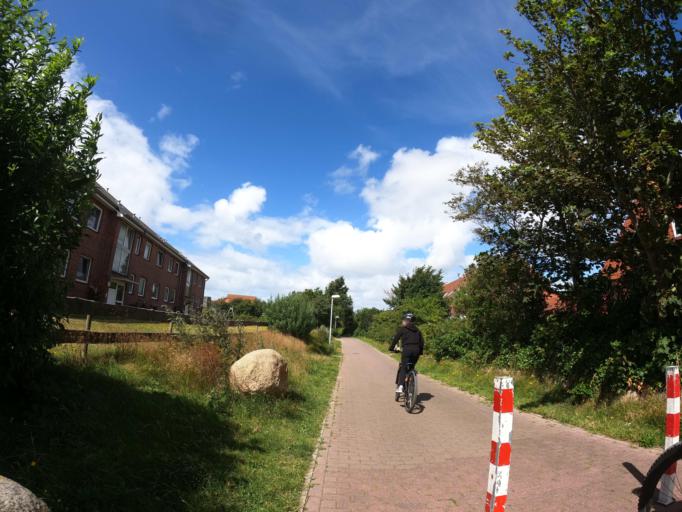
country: DE
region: Schleswig-Holstein
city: Westerland
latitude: 54.9005
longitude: 8.3135
